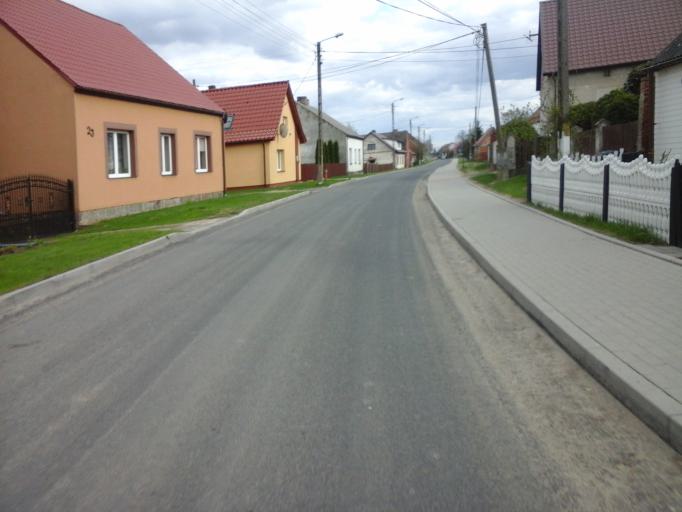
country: PL
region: West Pomeranian Voivodeship
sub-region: Powiat choszczenski
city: Krzecin
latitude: 53.0841
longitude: 15.5516
